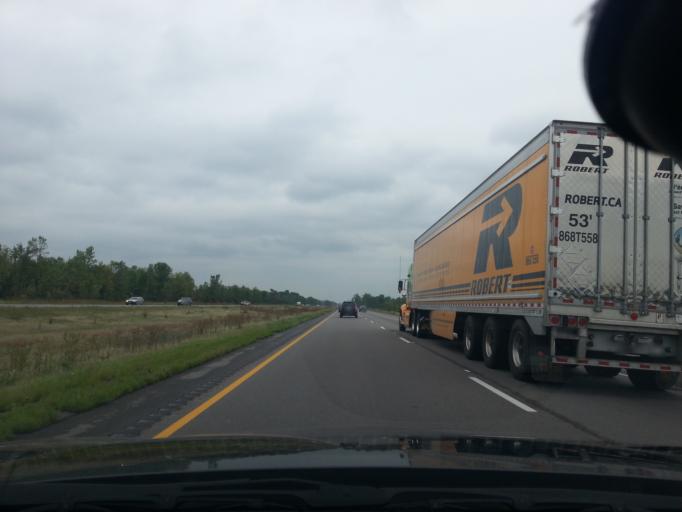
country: CA
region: Ontario
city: Skatepark
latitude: 44.2808
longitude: -76.7462
